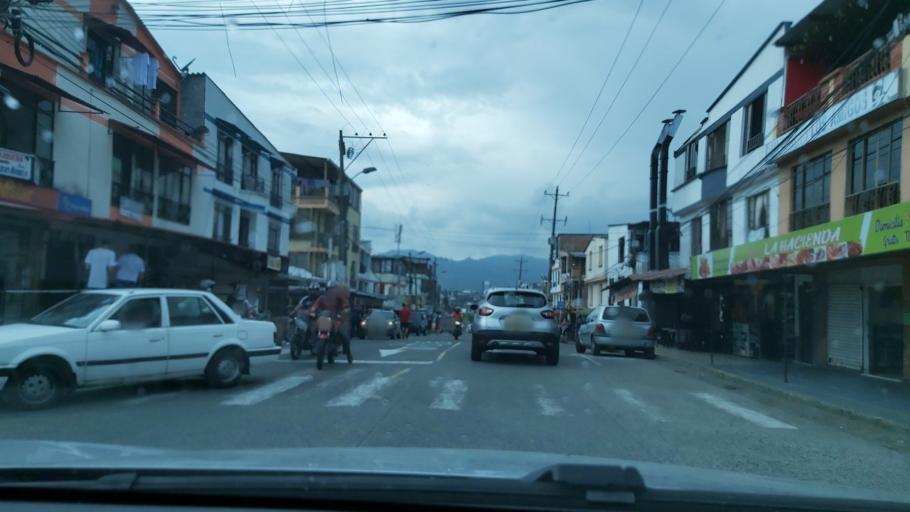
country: CO
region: Risaralda
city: Pereira
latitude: 4.7960
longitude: -75.7087
